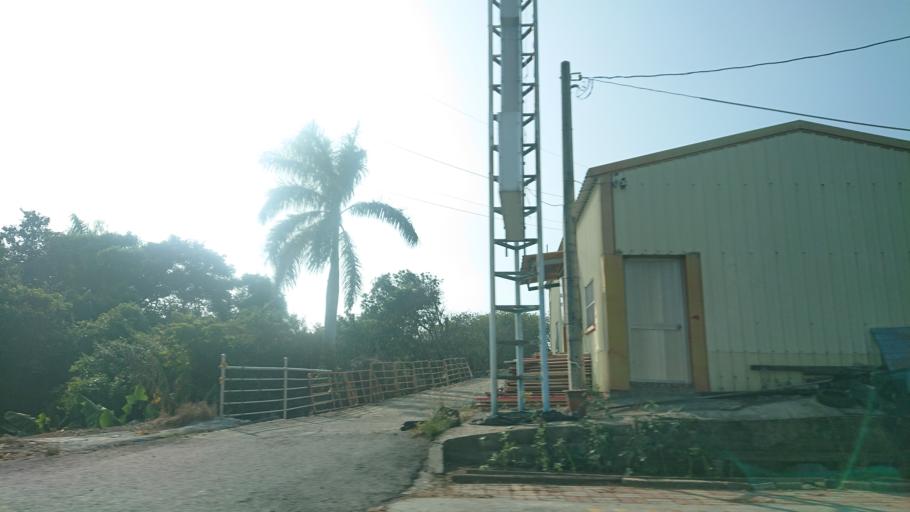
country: TW
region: Taiwan
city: Xinying
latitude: 23.3358
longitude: 120.2504
